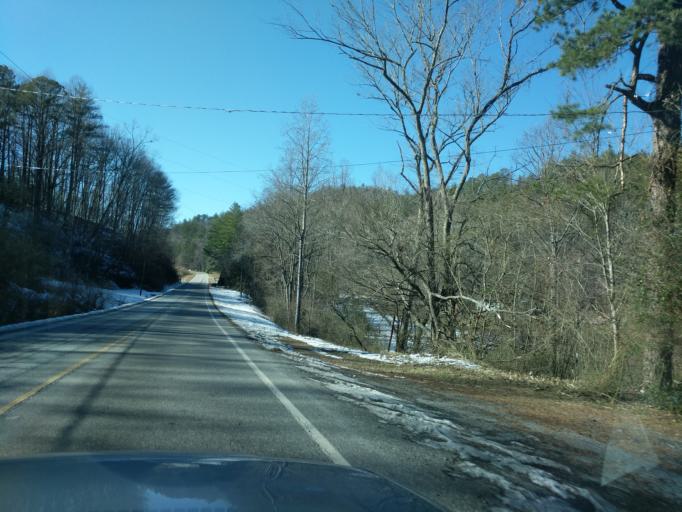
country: US
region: Georgia
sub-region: Rabun County
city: Clayton
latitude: 34.8680
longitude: -83.4730
